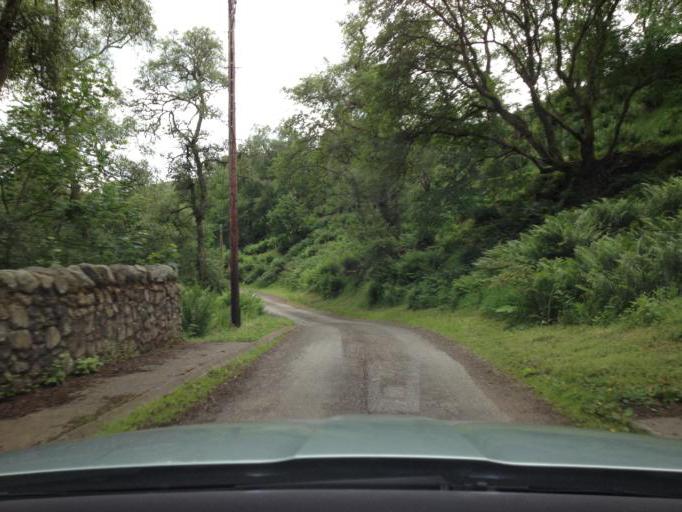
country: GB
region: Scotland
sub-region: Aberdeenshire
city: Aboyne
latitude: 56.9012
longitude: -2.7581
